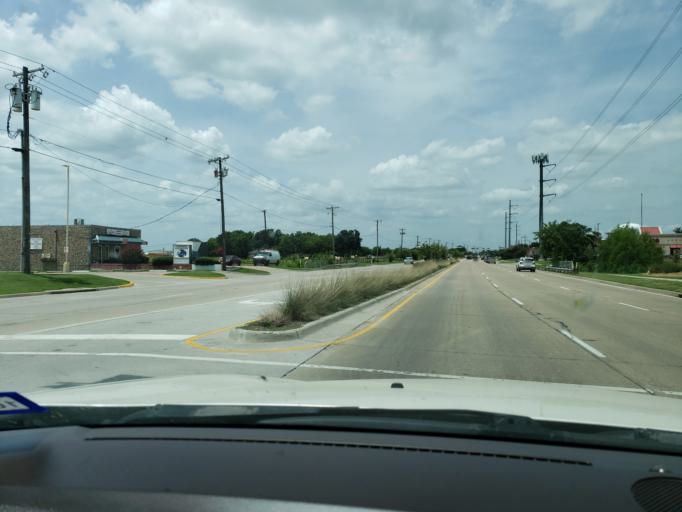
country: US
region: Texas
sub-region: Dallas County
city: Rowlett
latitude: 32.9076
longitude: -96.5730
